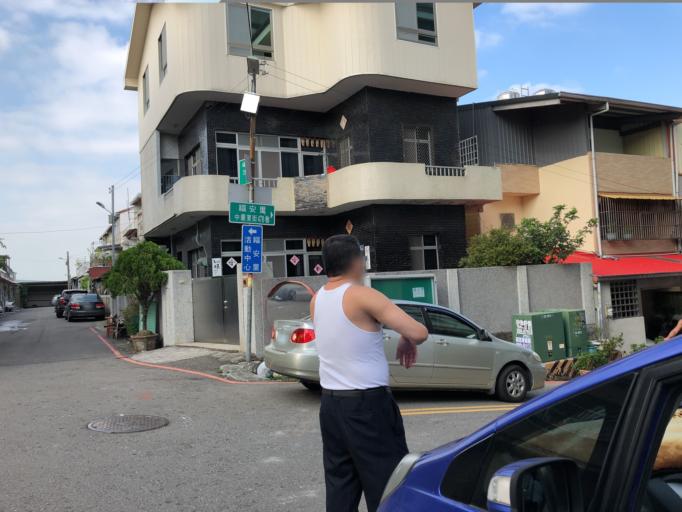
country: TW
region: Taiwan
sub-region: Miaoli
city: Miaoli
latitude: 24.5865
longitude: 120.8259
